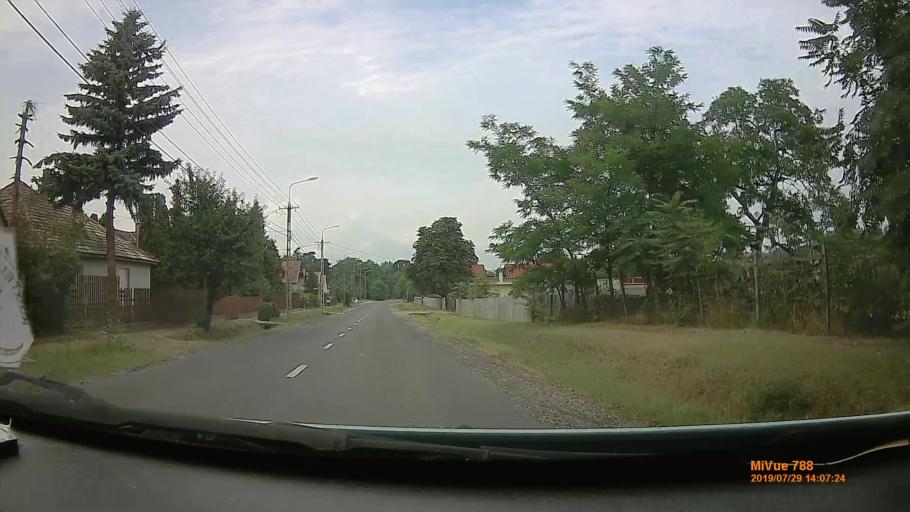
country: HU
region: Somogy
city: Balatonfoldvar
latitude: 46.8239
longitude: 17.9042
